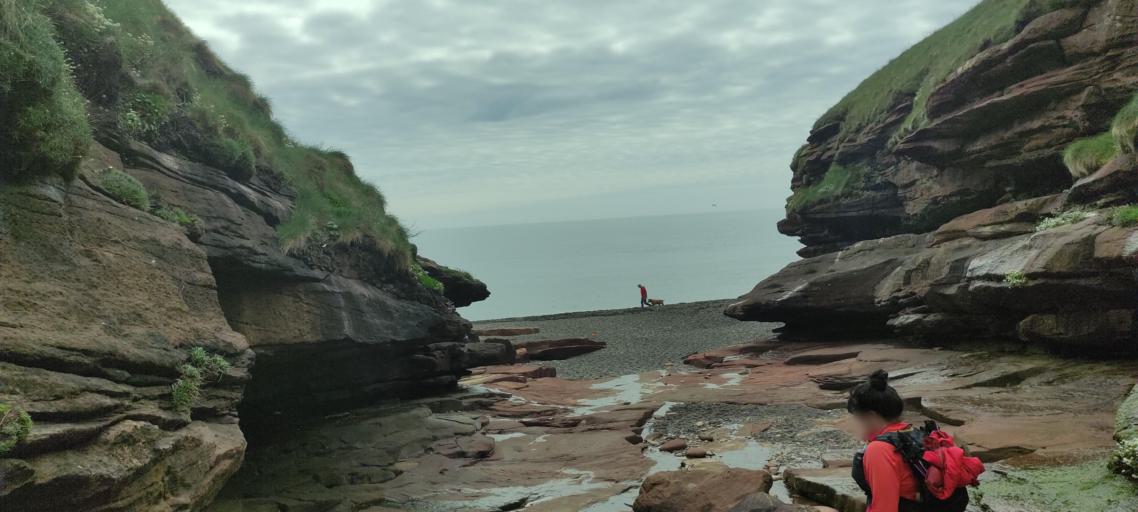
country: GB
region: England
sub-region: Cumbria
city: Saint Bees
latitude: 54.5048
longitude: -3.6304
